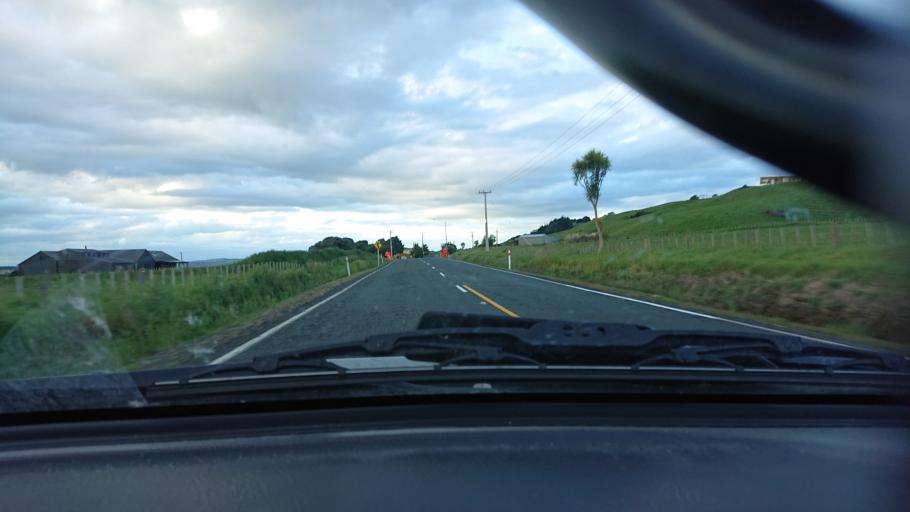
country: NZ
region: Auckland
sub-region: Auckland
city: Wellsford
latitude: -36.4517
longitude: 174.4341
